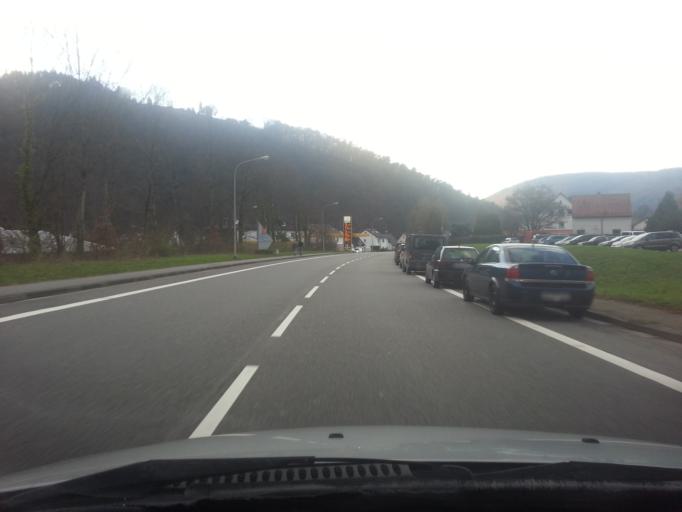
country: DE
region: Hesse
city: Neckarsteinach
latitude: 49.3985
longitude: 8.8473
